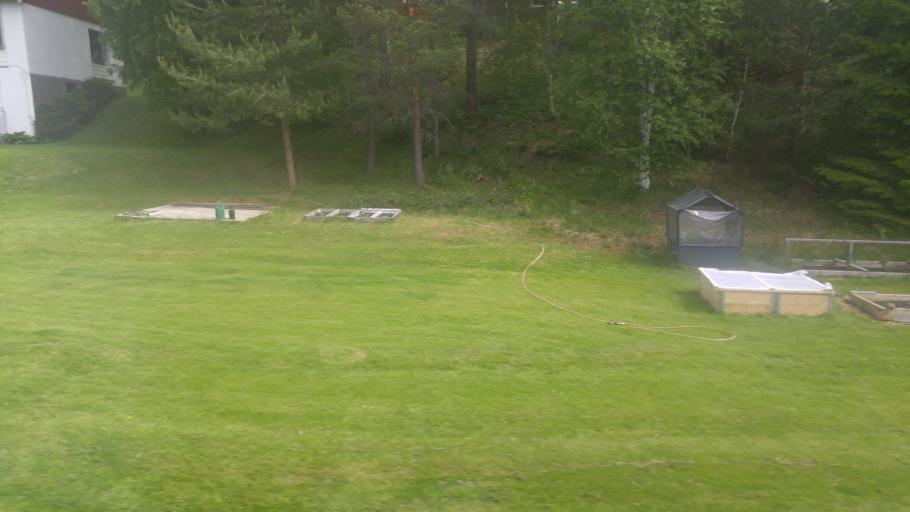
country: NO
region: Sor-Trondelag
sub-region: Selbu
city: Mebonden
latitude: 62.9618
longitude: 10.9747
